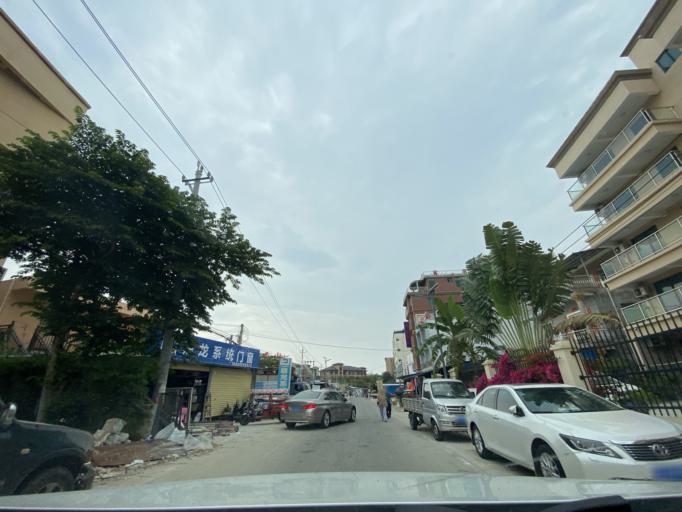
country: CN
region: Hainan
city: Yingzhou
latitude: 18.3907
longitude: 109.8433
